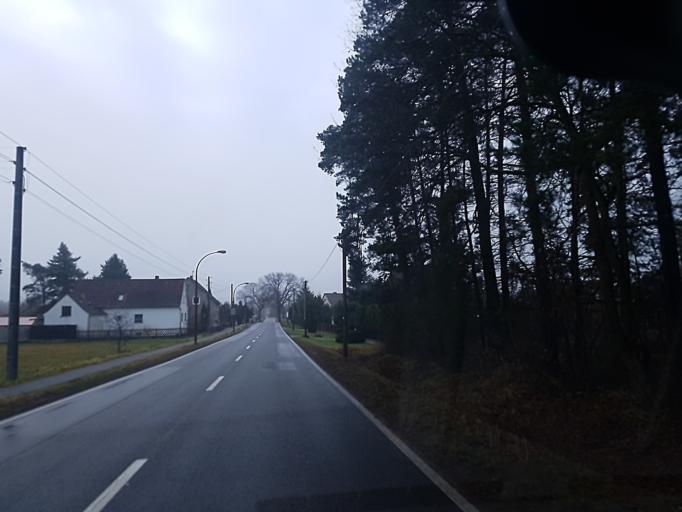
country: DE
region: Brandenburg
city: Finsterwalde
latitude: 51.5901
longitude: 13.7055
